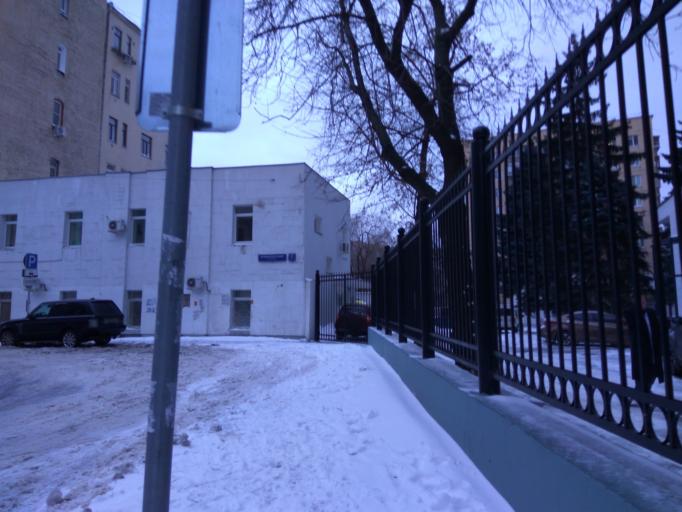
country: RU
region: Moskovskaya
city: Dorogomilovo
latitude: 55.7483
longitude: 37.5911
